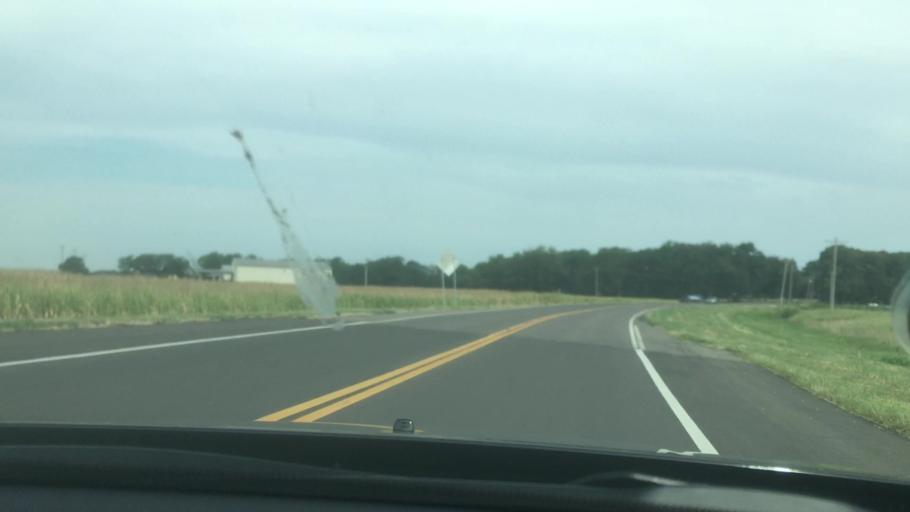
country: US
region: Oklahoma
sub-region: Garvin County
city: Pauls Valley
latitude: 34.7401
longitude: -97.2757
